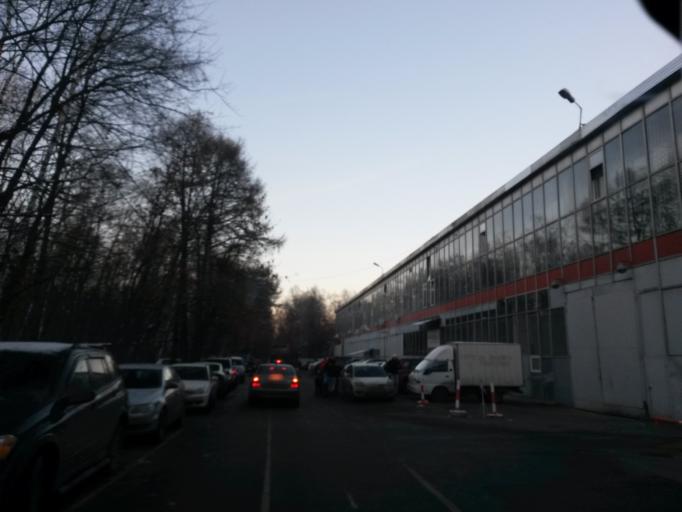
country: RU
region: Moscow
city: Sokol'niki
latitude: 55.8009
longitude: 37.6723
